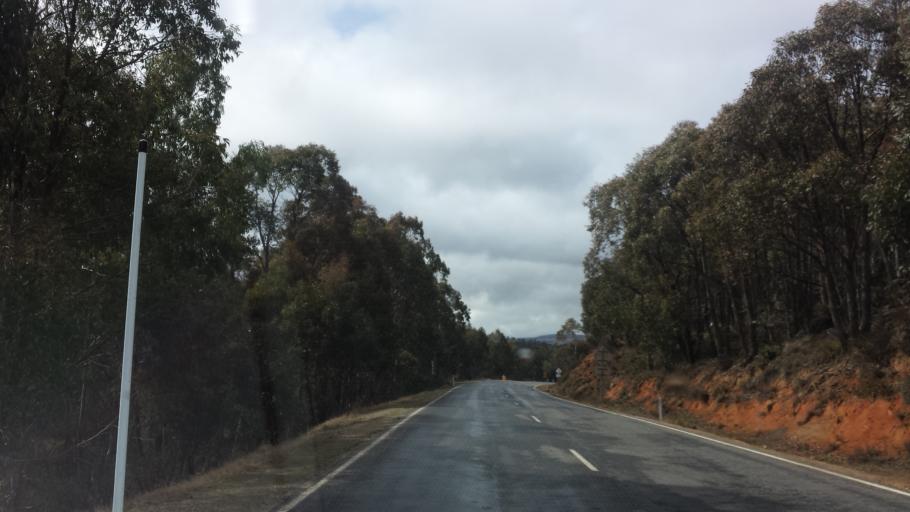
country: AU
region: Victoria
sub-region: Alpine
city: Mount Beauty
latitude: -37.0827
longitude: 147.3766
